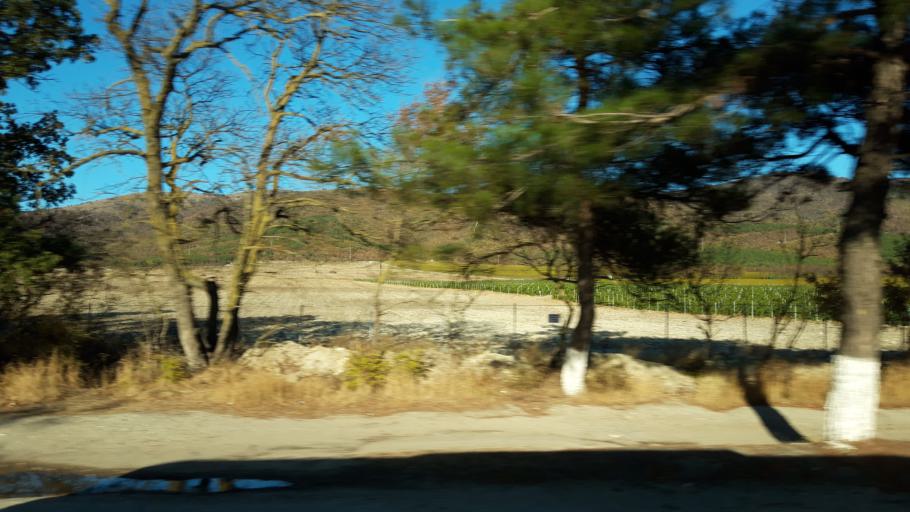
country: RU
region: Krasnodarskiy
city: Kabardinka
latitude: 44.6276
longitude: 38.0059
